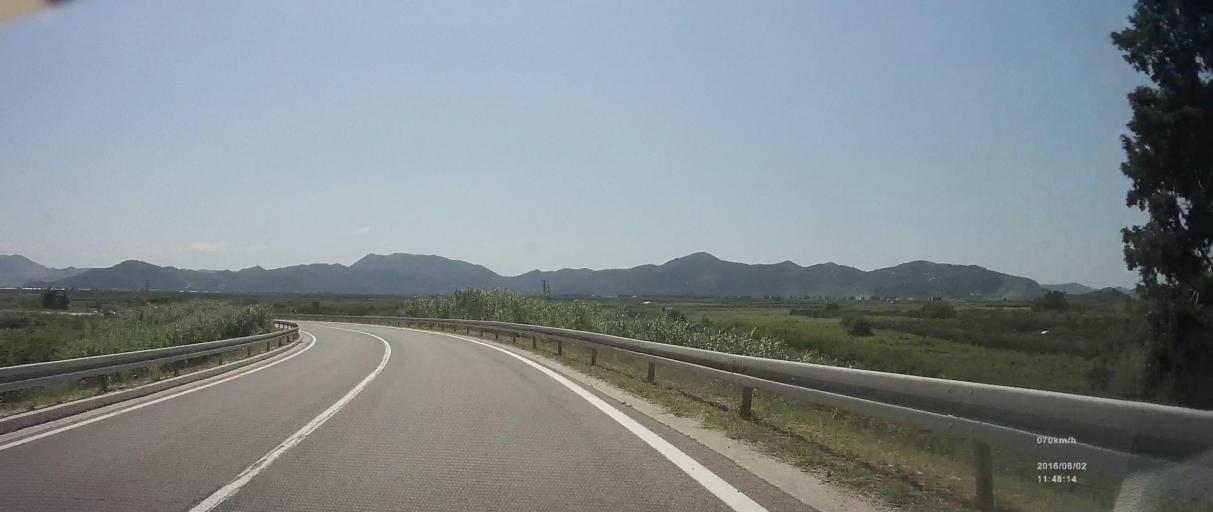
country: HR
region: Dubrovacko-Neretvanska
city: Komin
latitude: 43.0354
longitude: 17.4866
